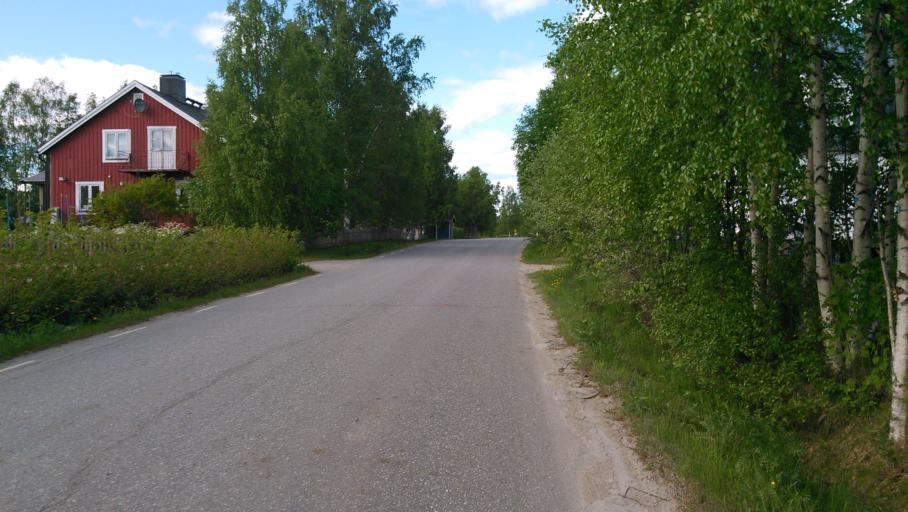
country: SE
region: Vaesterbotten
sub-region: Vannas Kommun
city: Vannasby
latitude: 63.9725
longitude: 19.8872
